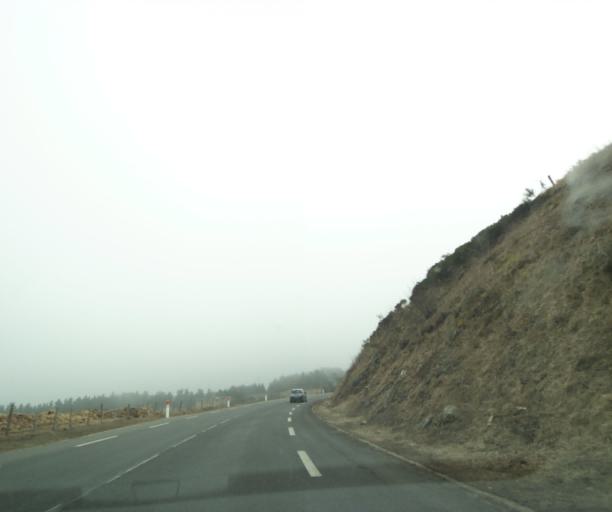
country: FR
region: Languedoc-Roussillon
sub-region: Departement de la Lozere
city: Langogne
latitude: 44.6753
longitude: 3.7669
